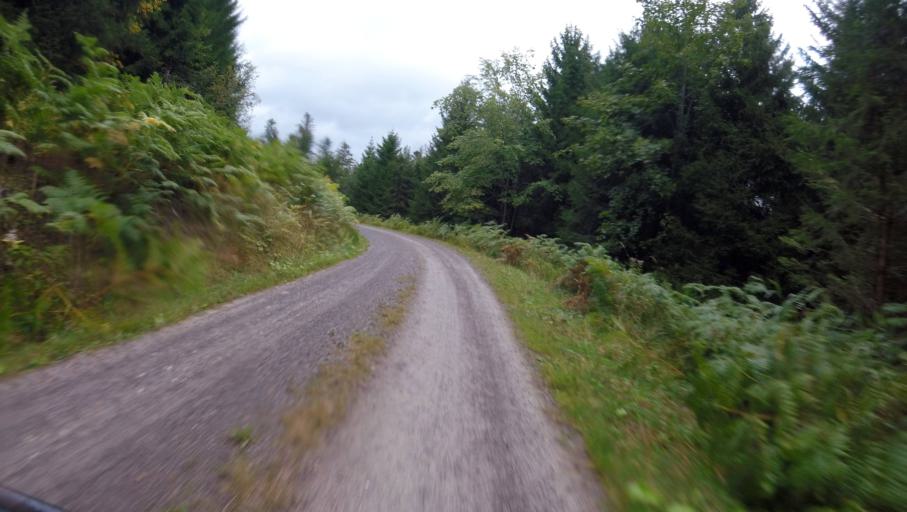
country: DE
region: Baden-Wuerttemberg
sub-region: Karlsruhe Region
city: Enzklosterle
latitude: 48.6683
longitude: 8.4230
